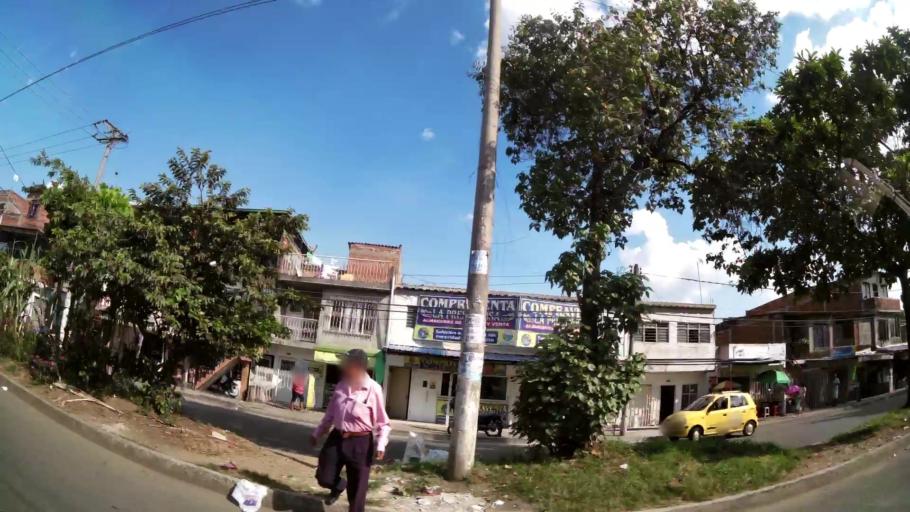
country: CO
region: Valle del Cauca
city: Cali
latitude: 3.4203
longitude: -76.4929
